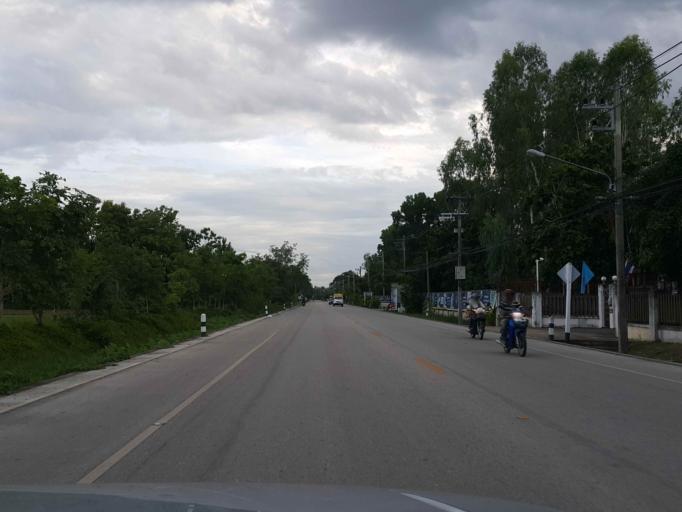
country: TH
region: Chiang Mai
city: San Sai
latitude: 18.8650
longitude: 99.1350
